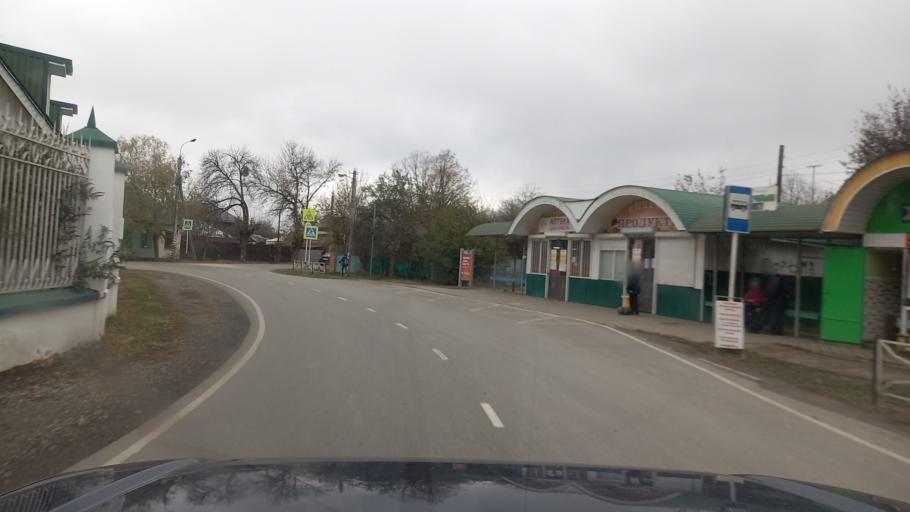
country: RU
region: Adygeya
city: Maykop
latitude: 44.6001
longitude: 40.0789
